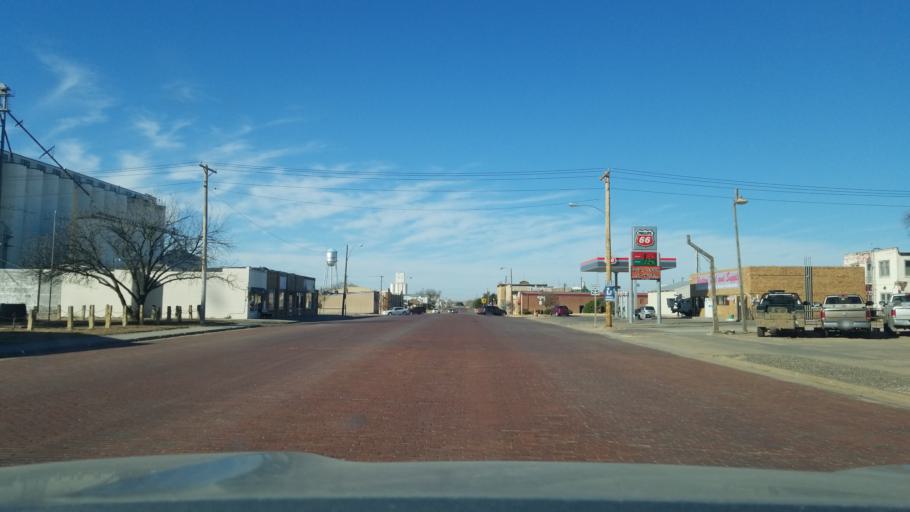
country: US
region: Kansas
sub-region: Ness County
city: Ness City
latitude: 38.4528
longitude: -99.9025
